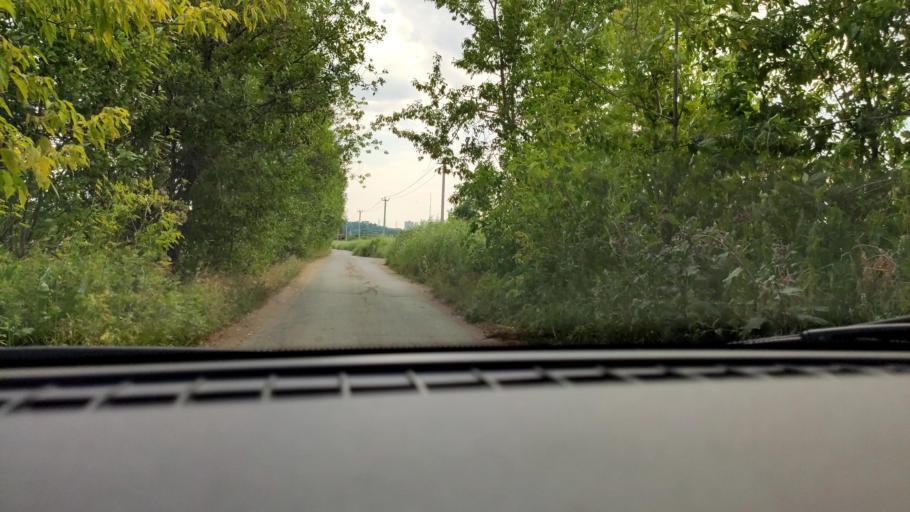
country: RU
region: Perm
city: Perm
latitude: 58.0300
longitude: 56.2341
